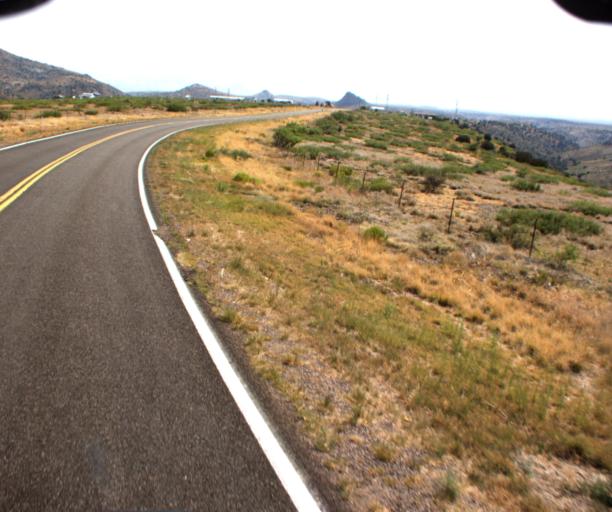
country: US
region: Arizona
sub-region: Greenlee County
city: Clifton
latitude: 33.0419
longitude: -109.1173
